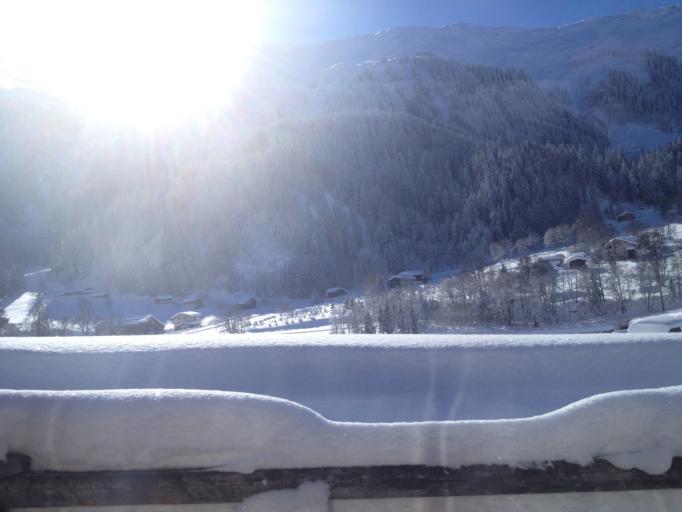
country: CH
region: Grisons
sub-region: Praettigau/Davos District
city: Klosters Serneus
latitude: 46.8624
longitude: 9.9131
